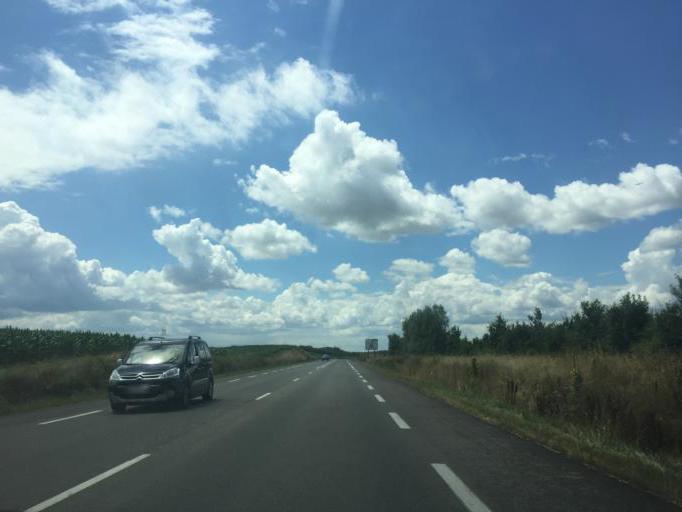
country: FR
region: Rhone-Alpes
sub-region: Departement de l'Isere
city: Janneyrias
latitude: 45.7694
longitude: 5.1223
